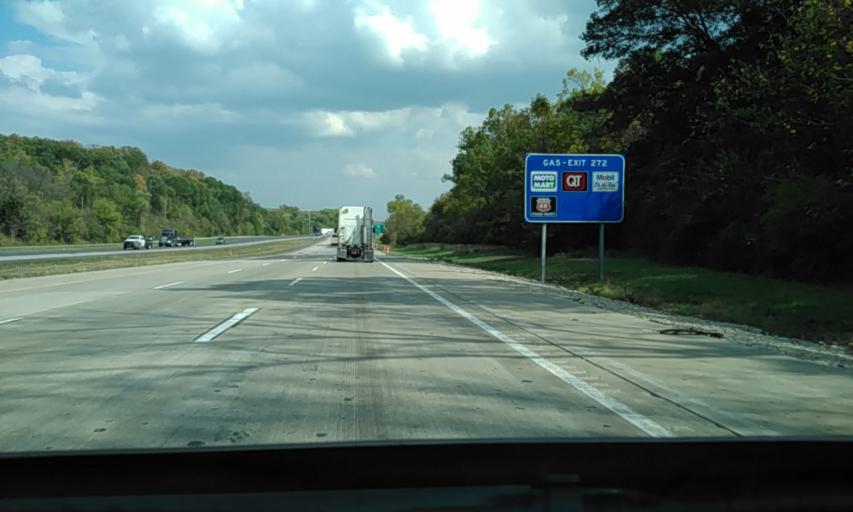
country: US
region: Missouri
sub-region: Saint Louis County
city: Valley Park
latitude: 38.5341
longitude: -90.5195
